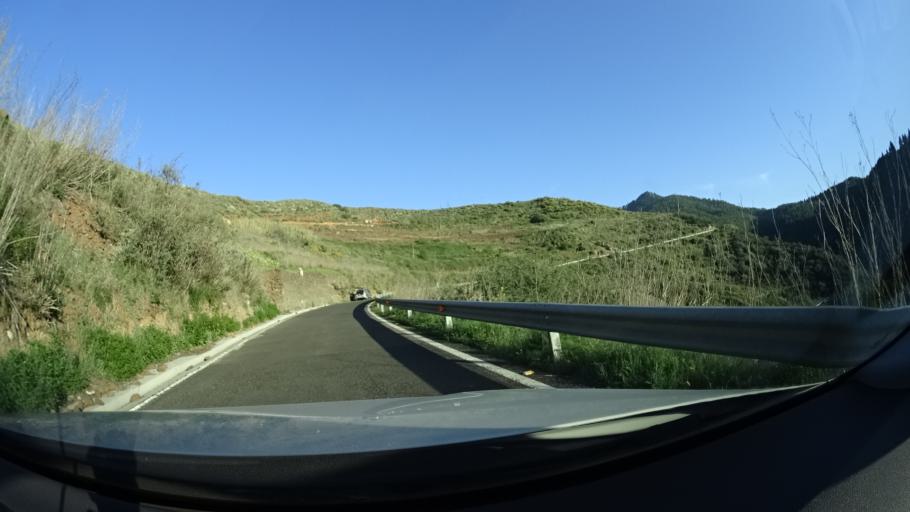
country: ES
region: Canary Islands
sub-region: Provincia de Las Palmas
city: Artenara
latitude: 28.0374
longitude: -15.6726
